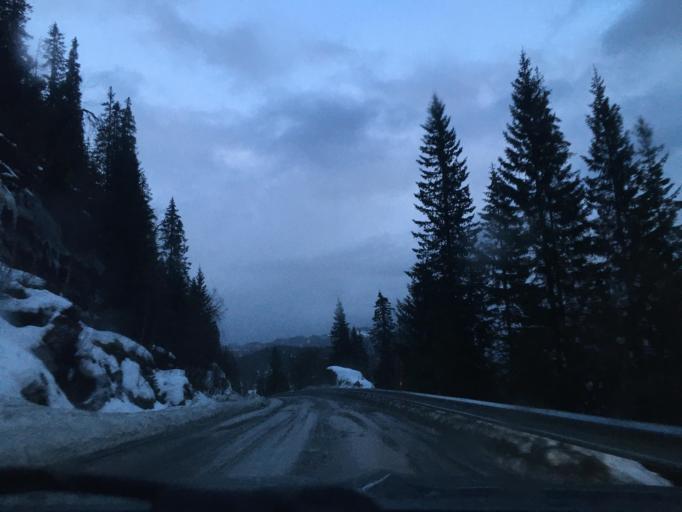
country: NO
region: Nordland
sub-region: Rana
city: Hauknes
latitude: 66.2978
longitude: 13.9235
